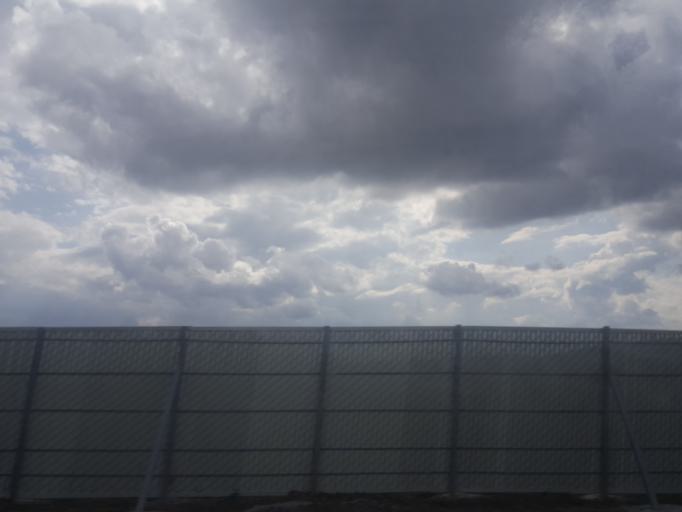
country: TR
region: Tokat
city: Bereketli
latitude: 40.5514
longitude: 37.3039
